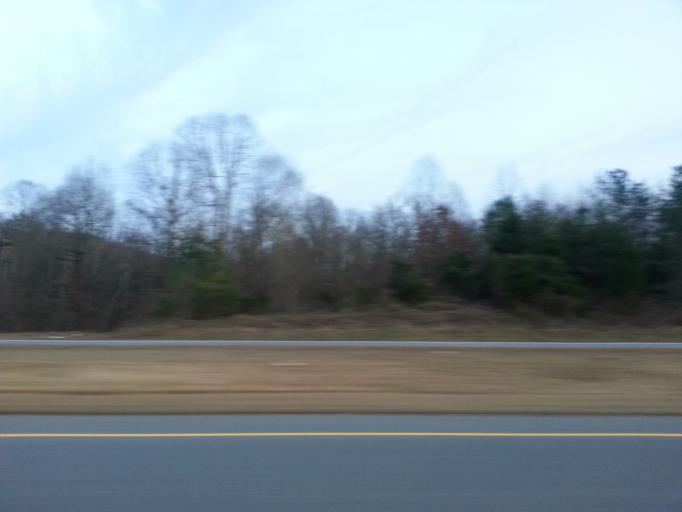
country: US
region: Tennessee
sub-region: McMinn County
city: Englewood
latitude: 35.3935
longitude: -84.5021
